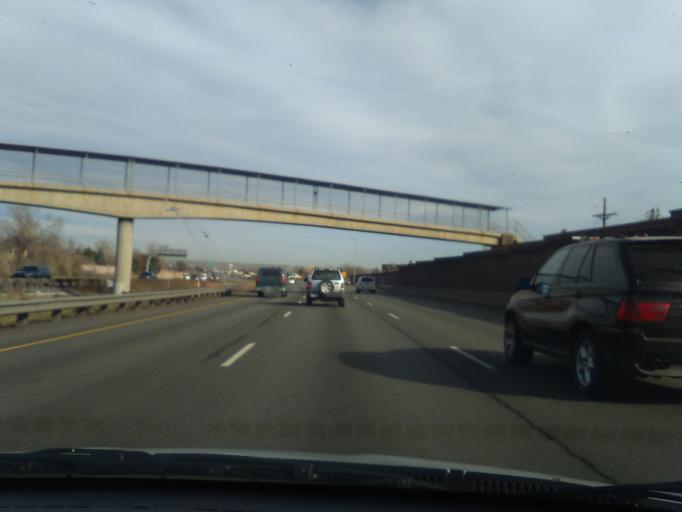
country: US
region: Colorado
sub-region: Jefferson County
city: Applewood
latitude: 39.7541
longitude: -105.1455
